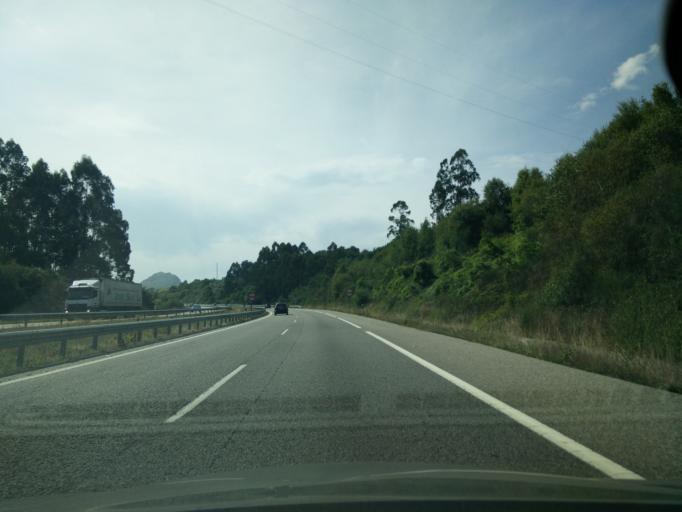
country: ES
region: Asturias
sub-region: Province of Asturias
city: Ribadesella
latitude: 43.4396
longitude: -5.0774
